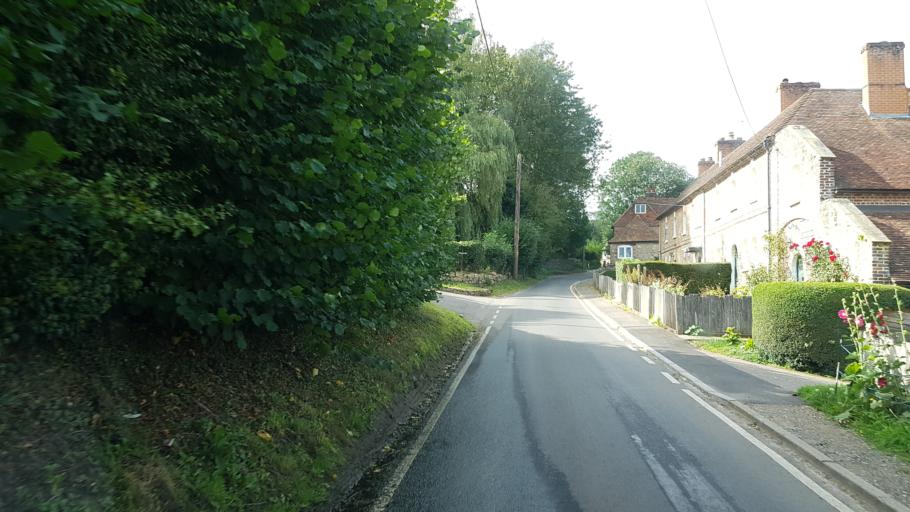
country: GB
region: England
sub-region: Kent
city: Harrietsham
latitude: 51.2424
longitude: 0.6338
